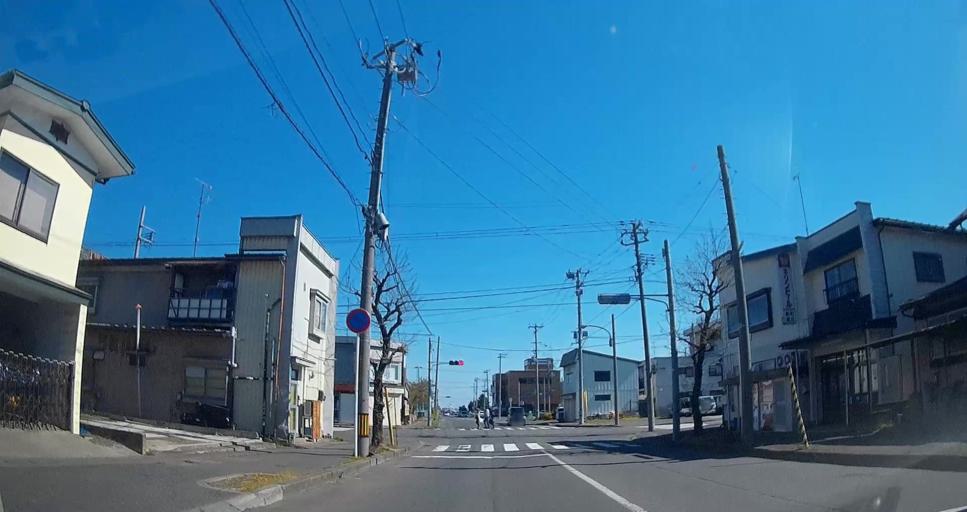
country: JP
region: Aomori
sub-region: Hachinohe Shi
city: Uchimaru
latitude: 40.5251
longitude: 141.5310
